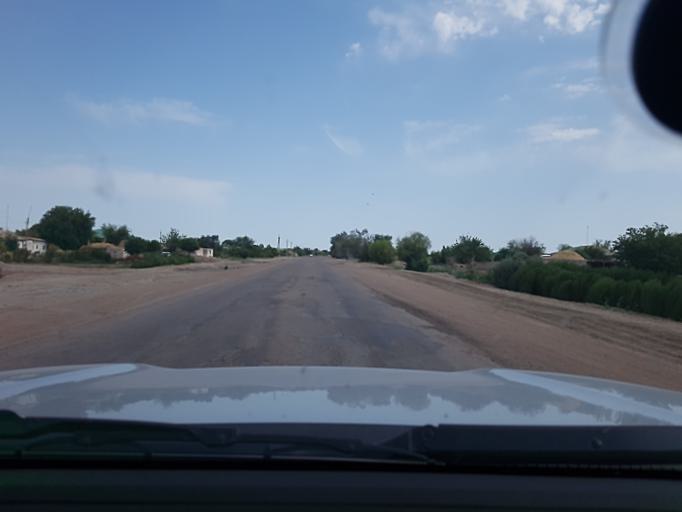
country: TM
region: Dasoguz
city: Boldumsaz
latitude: 42.0200
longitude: 59.8403
